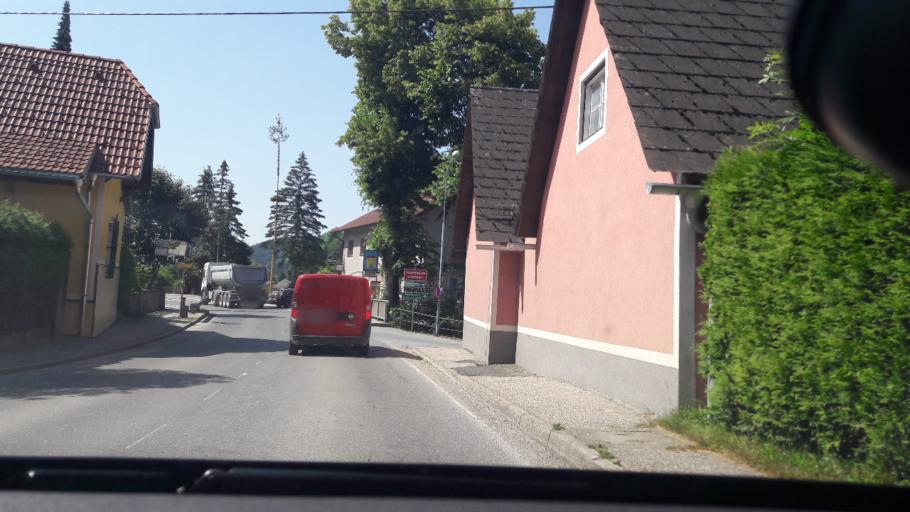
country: AT
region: Styria
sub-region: Politischer Bezirk Voitsberg
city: Kohlschwarz
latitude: 47.1082
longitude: 15.1204
